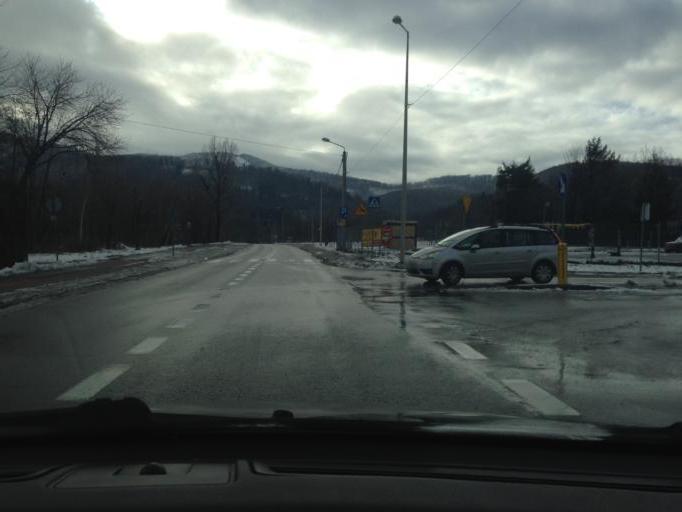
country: PL
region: Silesian Voivodeship
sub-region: Powiat bielski
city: Bystra
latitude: 49.7830
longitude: 19.0274
